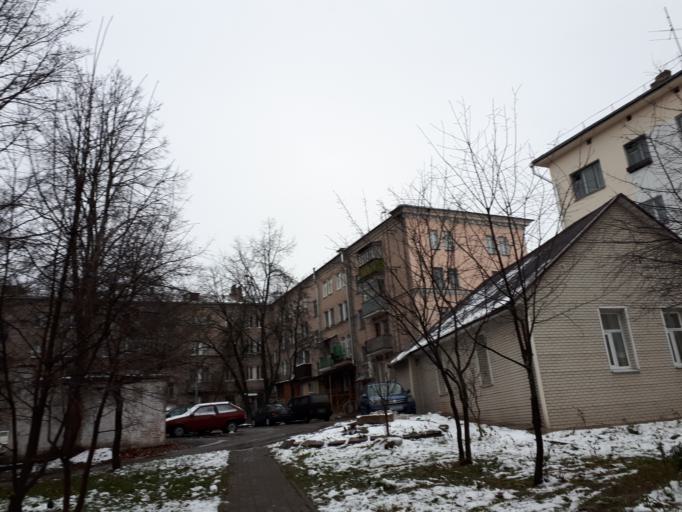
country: BY
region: Vitebsk
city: Vitebsk
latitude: 55.1987
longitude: 30.2087
